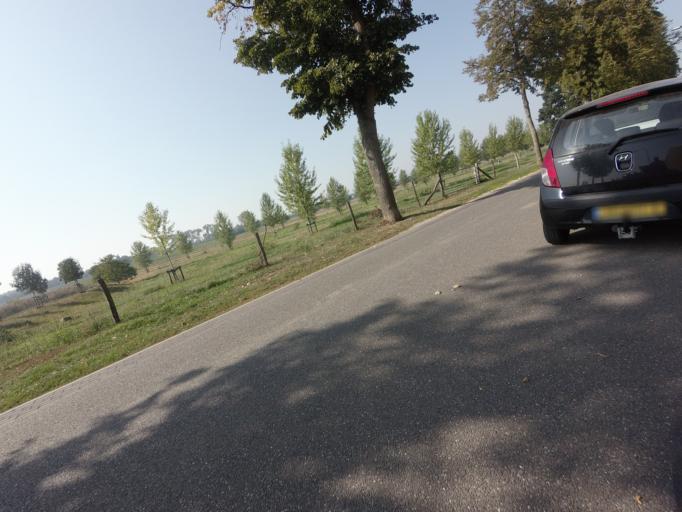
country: NL
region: Limburg
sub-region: Gemeente Roermond
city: Leeuwen
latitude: 51.2307
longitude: 5.9826
